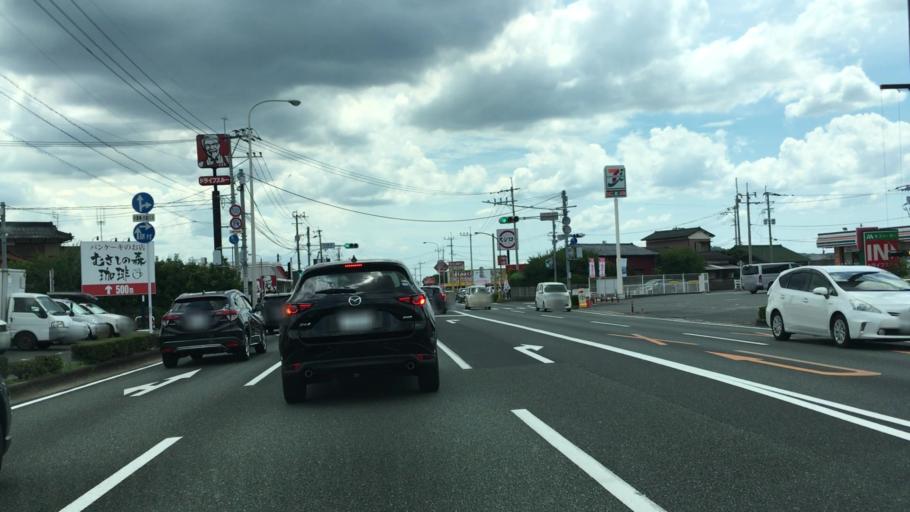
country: JP
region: Saga Prefecture
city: Tosu
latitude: 33.3881
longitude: 130.4999
